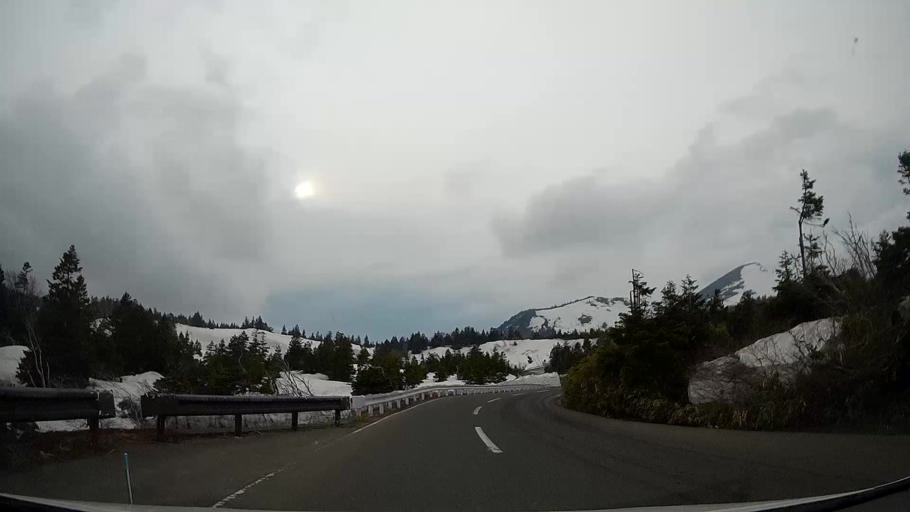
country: JP
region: Aomori
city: Aomori Shi
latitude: 40.6317
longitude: 140.8885
